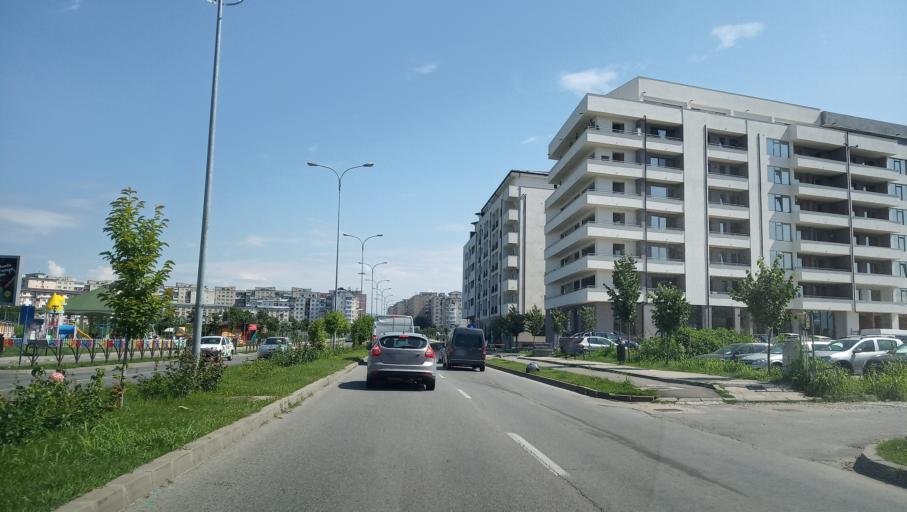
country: RO
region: Valcea
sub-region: Municipiul Ramnicu Valcea
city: Ramnicu Valcea
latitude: 45.0878
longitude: 24.3695
